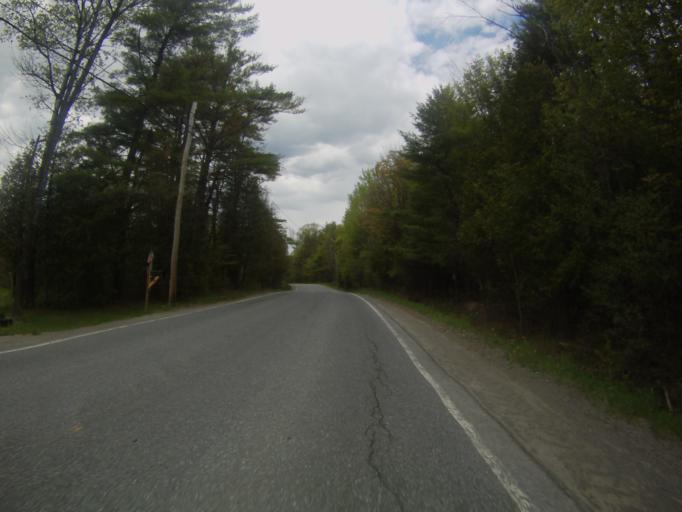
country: US
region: New York
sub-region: Essex County
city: Port Henry
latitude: 43.9968
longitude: -73.4946
